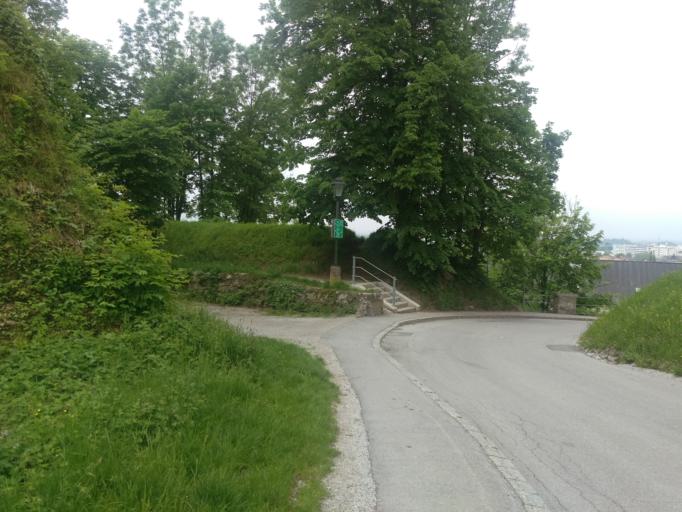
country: AT
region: Salzburg
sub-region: Salzburg Stadt
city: Salzburg
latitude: 47.8049
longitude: 13.0350
